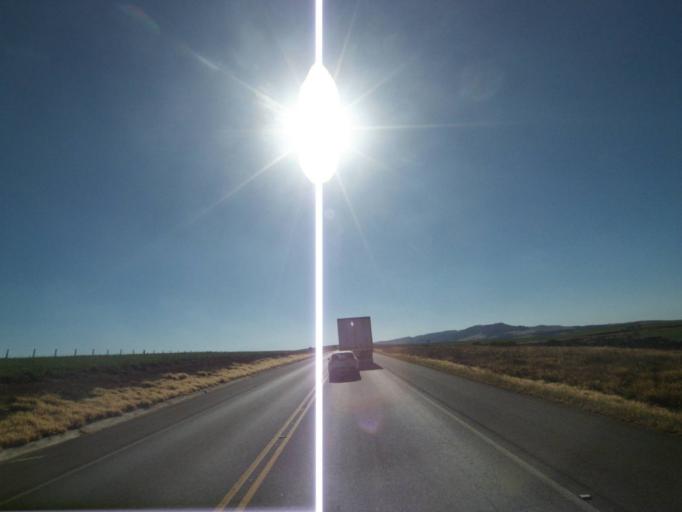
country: BR
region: Parana
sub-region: Tibagi
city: Tibagi
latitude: -24.6387
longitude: -50.4590
